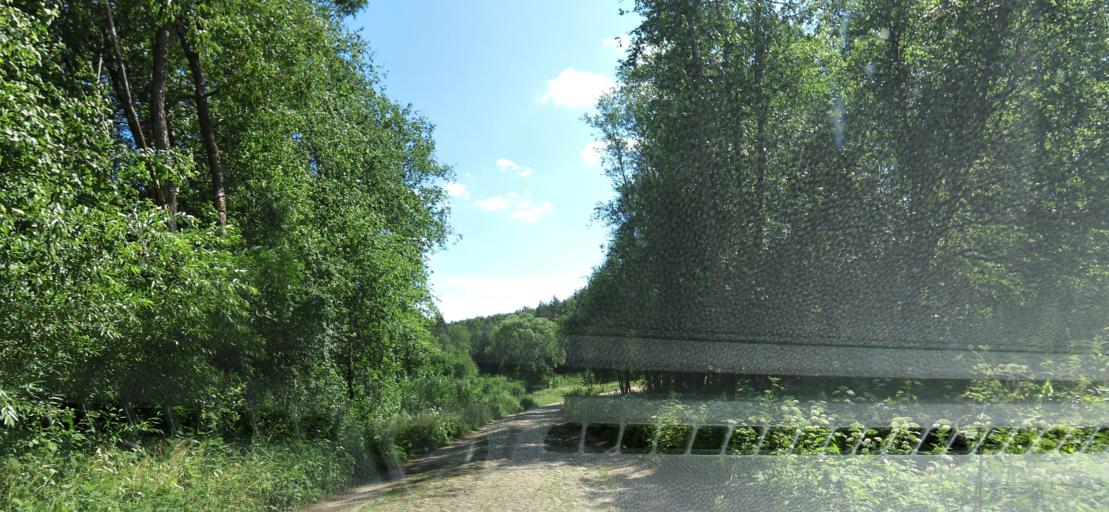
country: LT
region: Vilnius County
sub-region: Vilnius
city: Fabijoniskes
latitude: 54.8311
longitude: 25.3242
